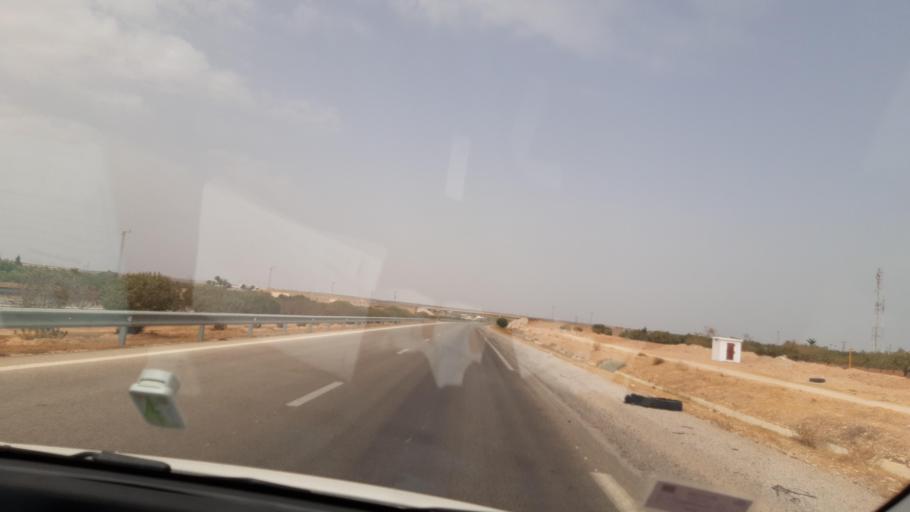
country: TN
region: Safaqis
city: Sfax
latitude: 34.8710
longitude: 10.6941
